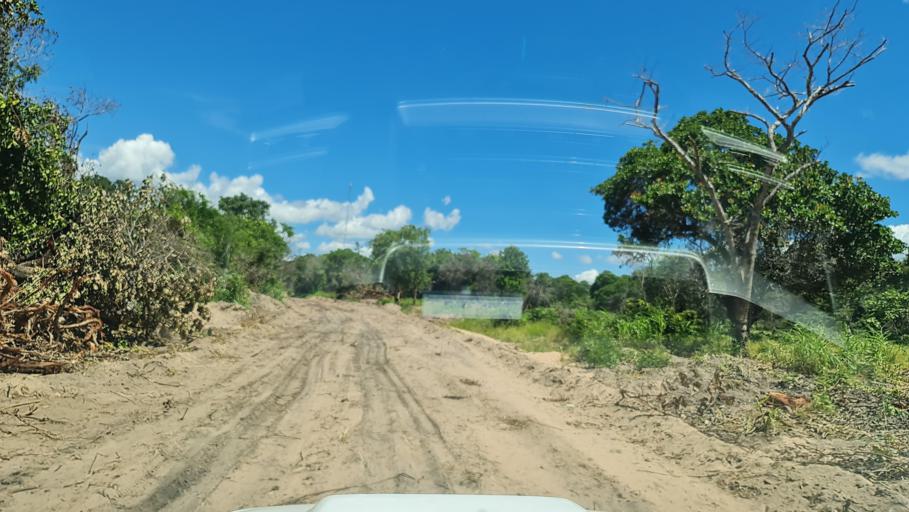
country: MZ
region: Nampula
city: Nampula
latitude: -15.3027
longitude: 39.8752
